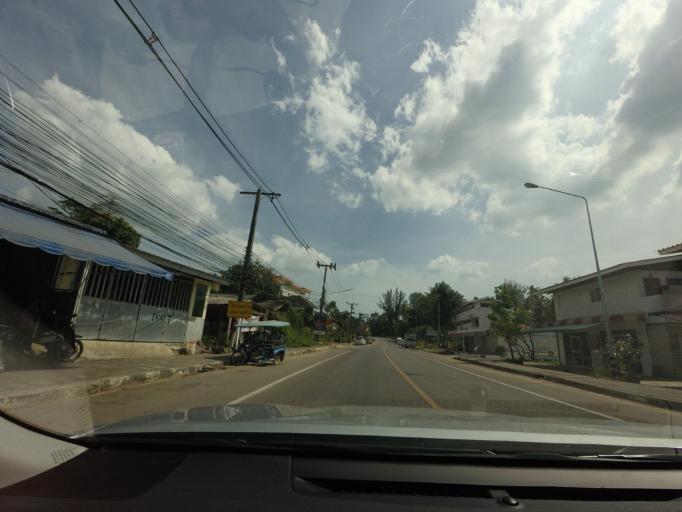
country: TH
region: Phangnga
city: Ban Ao Nang
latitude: 8.0572
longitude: 98.7495
